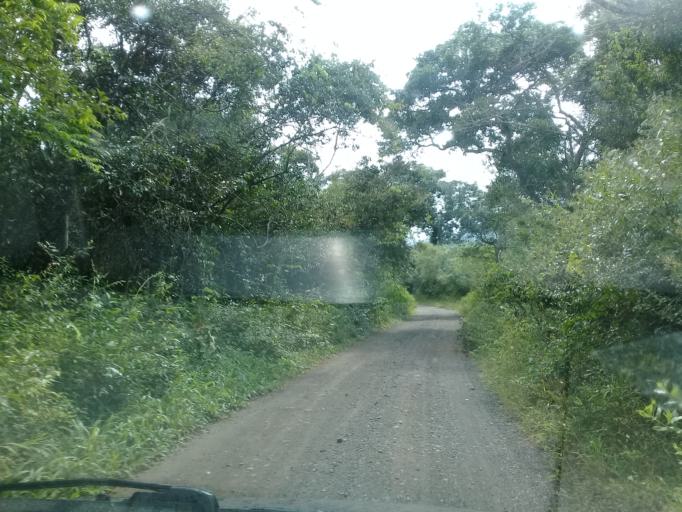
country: CO
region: Cundinamarca
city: Guaduas
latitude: 5.0904
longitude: -74.6080
